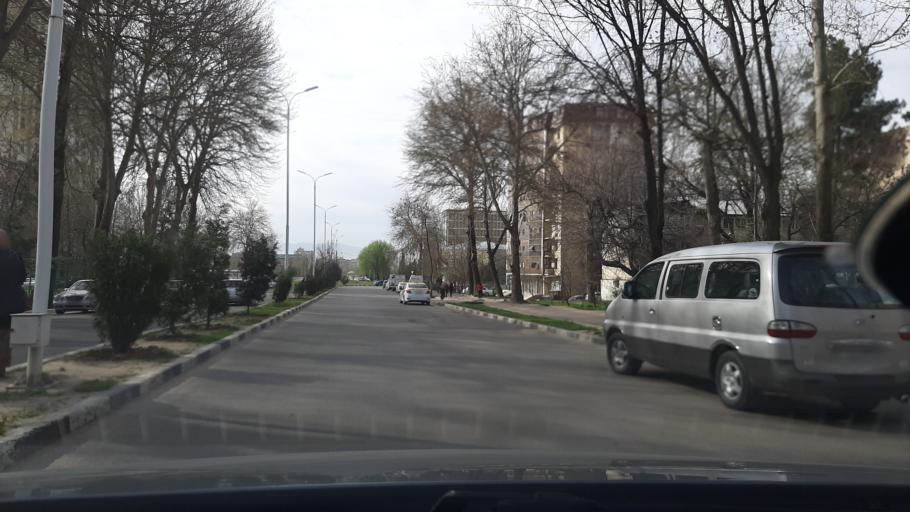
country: TJ
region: Dushanbe
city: Dushanbe
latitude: 38.5794
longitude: 68.7490
